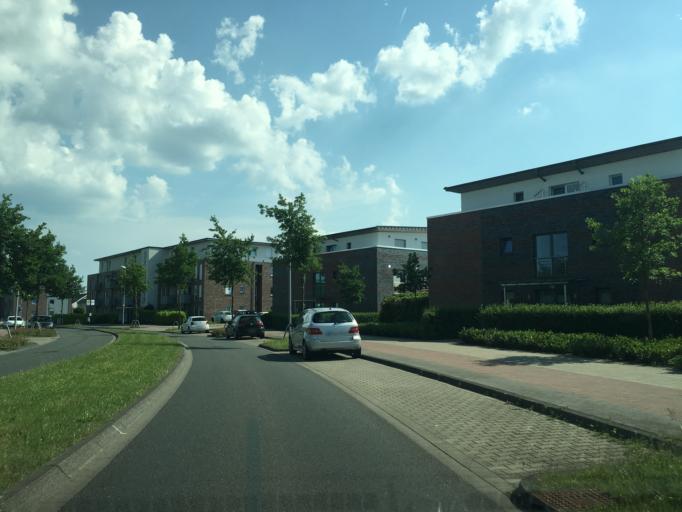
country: DE
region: North Rhine-Westphalia
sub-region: Regierungsbezirk Munster
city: Muenster
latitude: 51.9624
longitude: 7.5666
